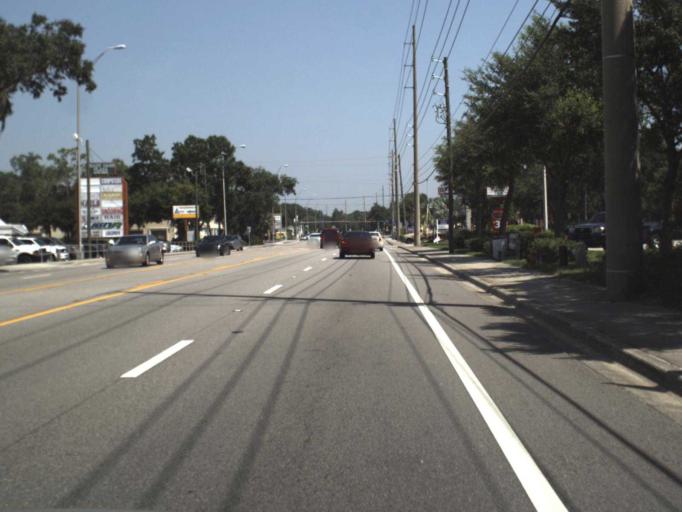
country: US
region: Florida
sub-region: Hillsborough County
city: Lake Magdalene
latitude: 28.0846
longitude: -82.4595
